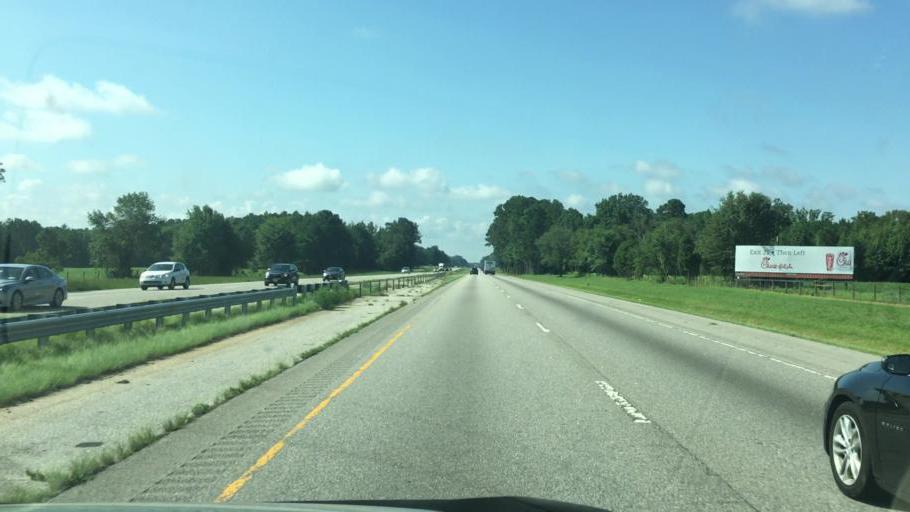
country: US
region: North Carolina
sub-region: Robeson County
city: Saint Pauls
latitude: 34.8794
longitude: -78.9621
